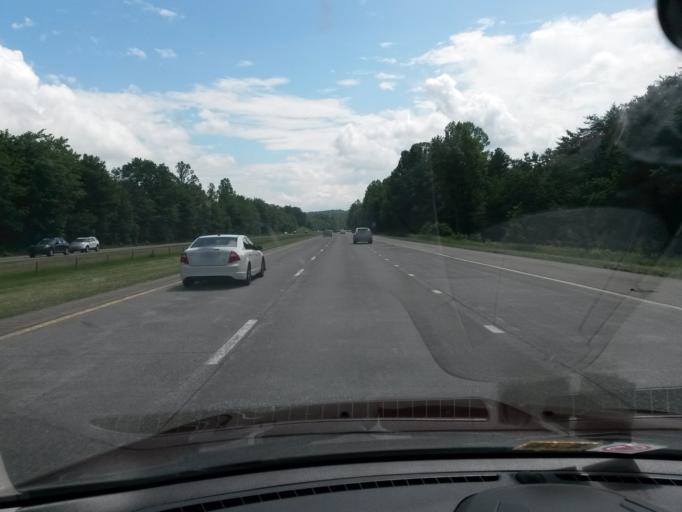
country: US
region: North Carolina
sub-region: Surry County
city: Dobson
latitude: 36.4769
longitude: -80.7535
